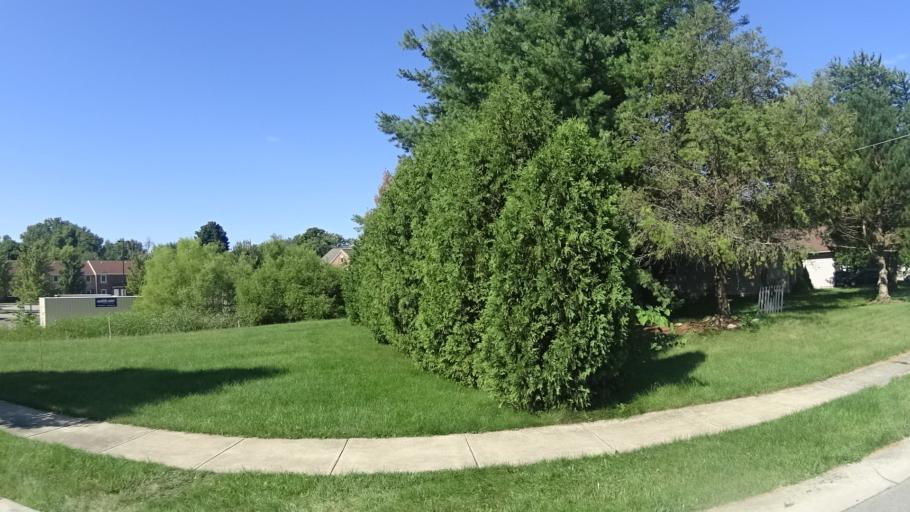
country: US
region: Indiana
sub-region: Madison County
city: Pendleton
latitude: 40.0049
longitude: -85.7341
